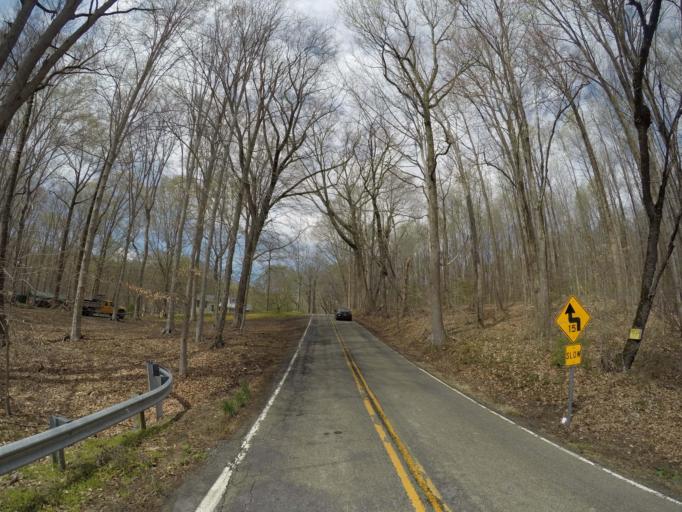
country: US
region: Maryland
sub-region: Cecil County
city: Perryville
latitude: 39.5865
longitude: -76.0515
